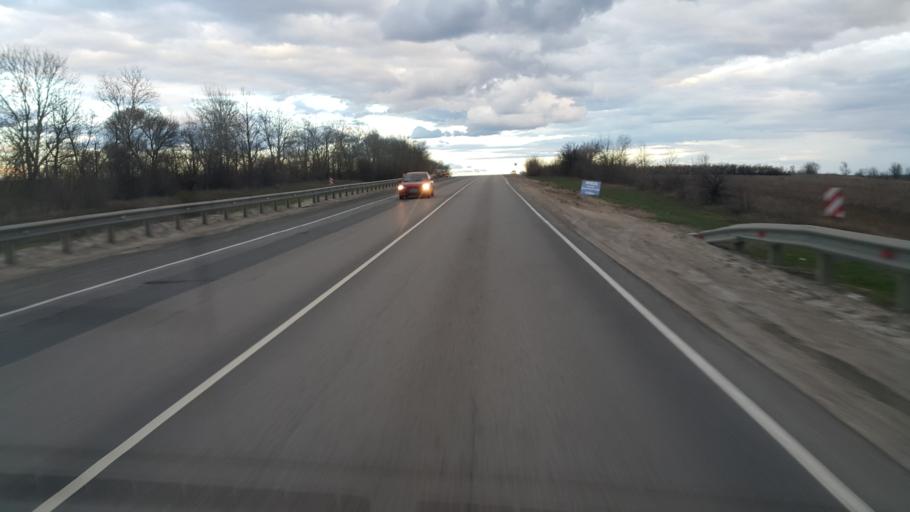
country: RU
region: Volgograd
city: Mikhaylovka
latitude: 49.9903
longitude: 43.2578
